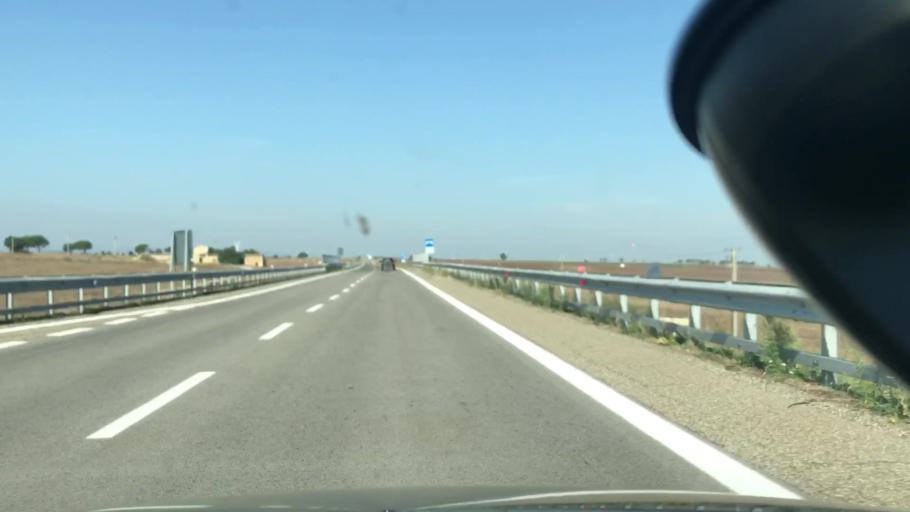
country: IT
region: Basilicate
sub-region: Provincia di Potenza
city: Montemilone
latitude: 40.9869
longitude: 15.9116
